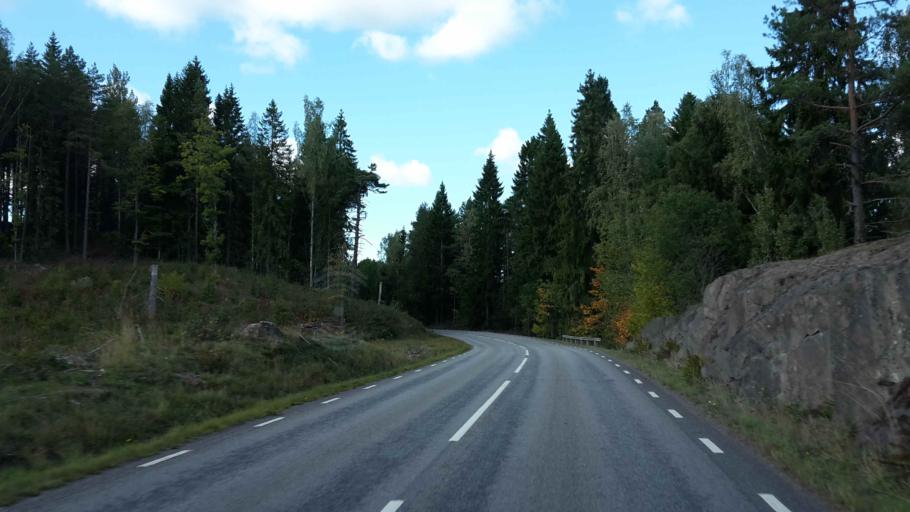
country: SE
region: OEstergoetland
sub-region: Atvidabergs Kommun
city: Atvidaberg
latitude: 58.1732
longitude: 16.1331
